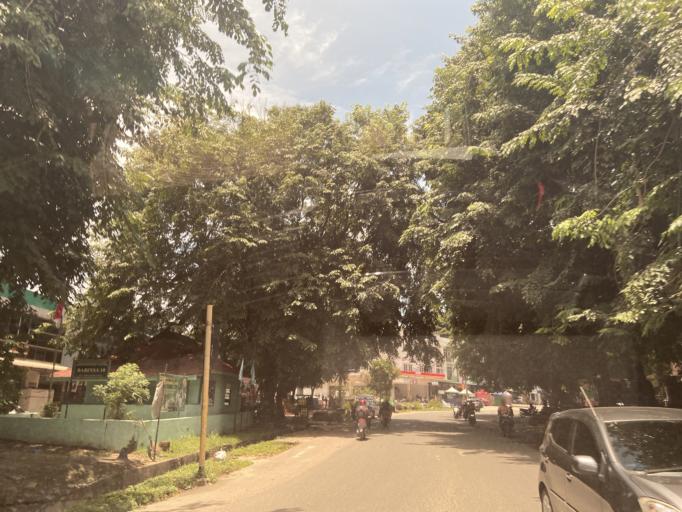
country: SG
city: Singapore
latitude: 1.1584
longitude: 104.0251
